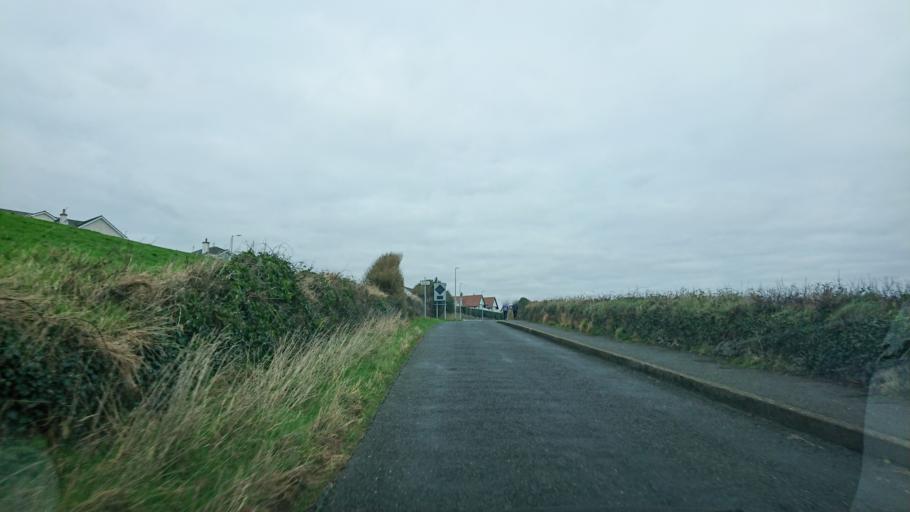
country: IE
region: Munster
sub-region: Waterford
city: Tra Mhor
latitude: 52.1473
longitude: -7.1637
